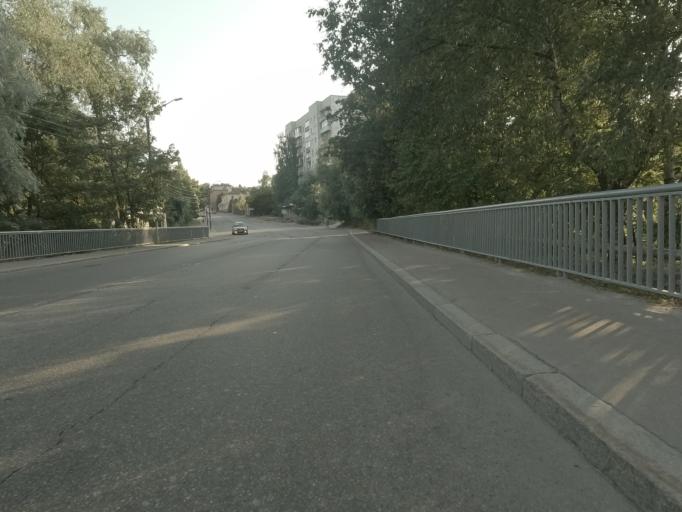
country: RU
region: Leningrad
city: Vyborg
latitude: 60.7200
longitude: 28.7645
